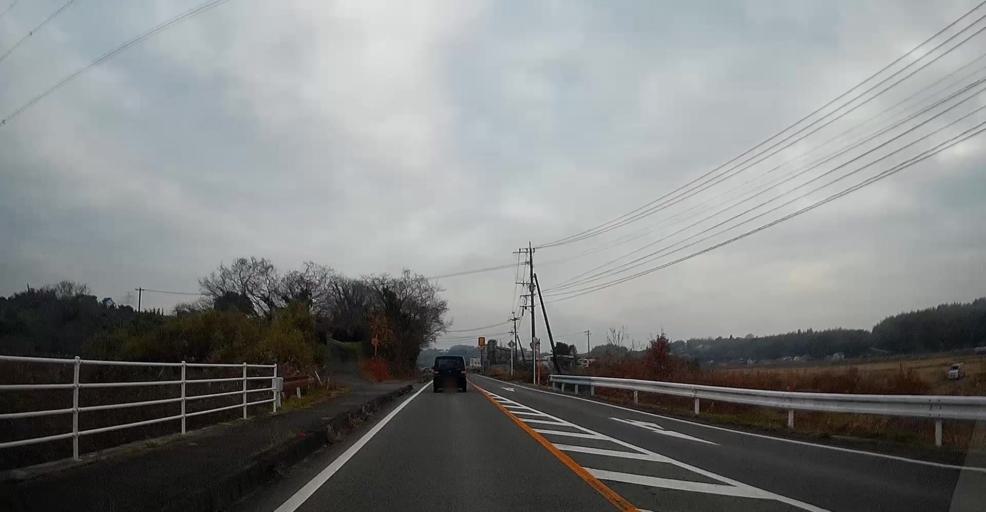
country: JP
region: Kumamoto
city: Yatsushiro
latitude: 32.6165
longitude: 130.5092
